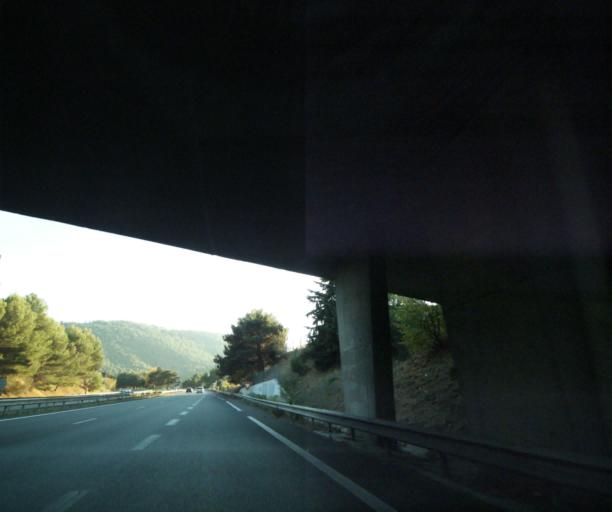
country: FR
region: Provence-Alpes-Cote d'Azur
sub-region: Departement des Bouches-du-Rhone
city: Aubagne
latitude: 43.2837
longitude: 5.5848
